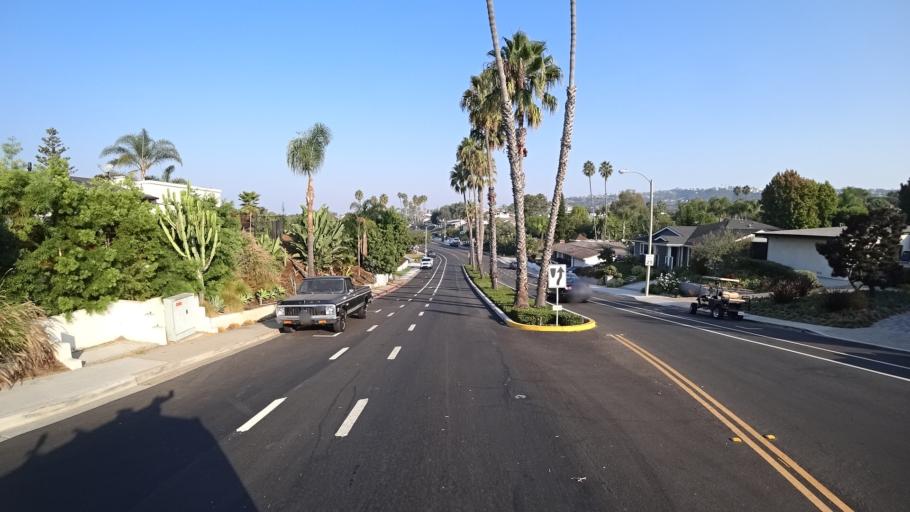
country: US
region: California
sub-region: Orange County
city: San Clemente
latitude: 33.4100
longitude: -117.6041
